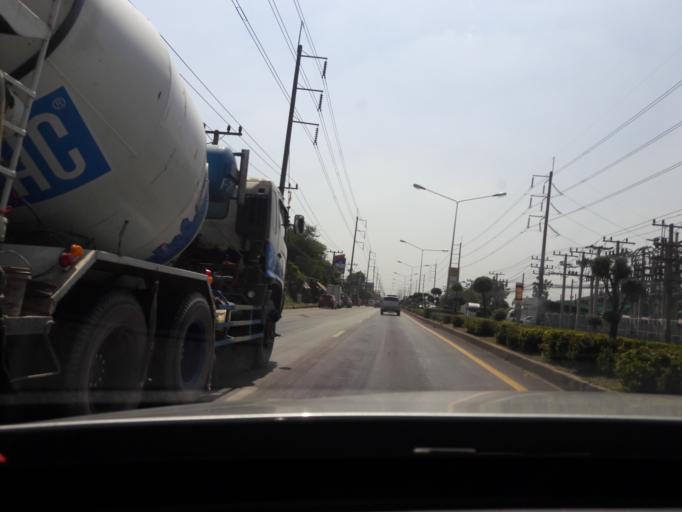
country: TH
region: Samut Sakhon
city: Krathum Baen
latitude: 13.6127
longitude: 100.2885
